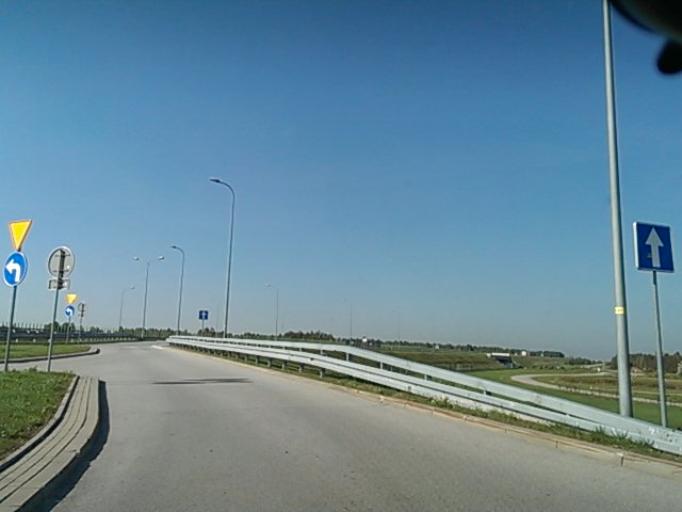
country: PL
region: Subcarpathian Voivodeship
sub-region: Powiat rzeszowski
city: Trzciana
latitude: 50.1113
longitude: 21.8434
